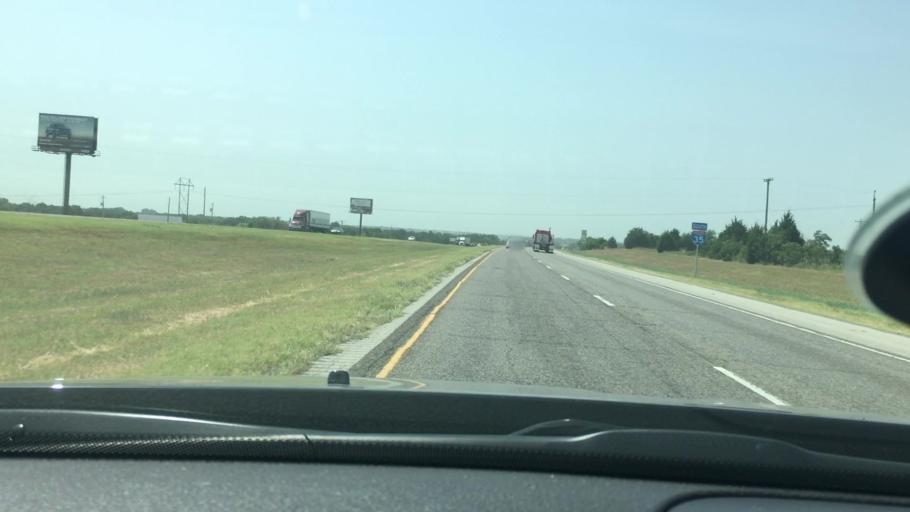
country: US
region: Oklahoma
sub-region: Garvin County
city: Wynnewood
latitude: 34.6142
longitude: -97.2139
